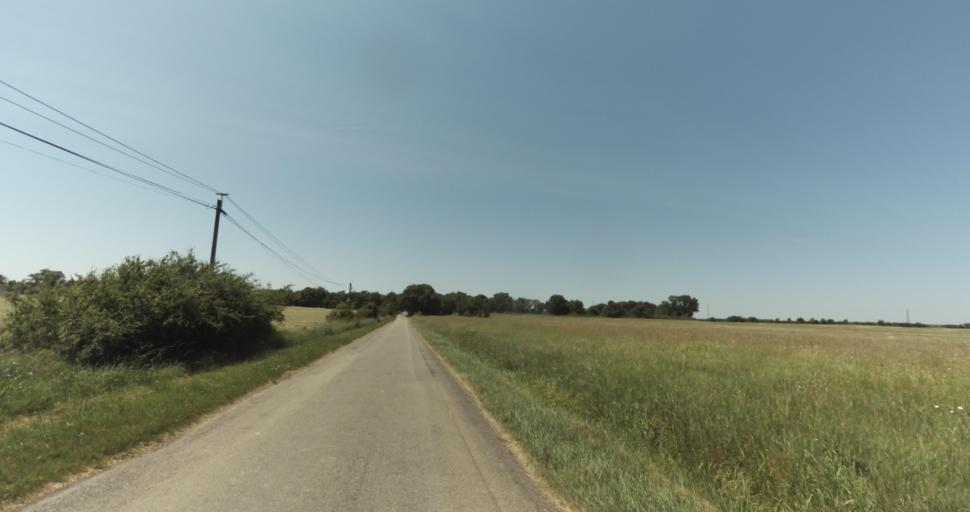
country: FR
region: Midi-Pyrenees
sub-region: Departement de la Haute-Garonne
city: Levignac
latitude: 43.6354
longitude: 1.1867
